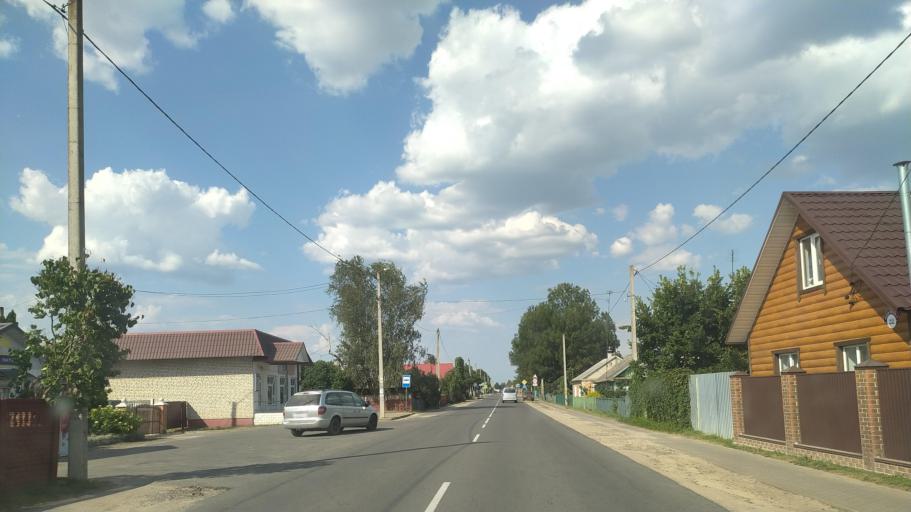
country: BY
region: Brest
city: Drahichyn
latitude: 52.1917
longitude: 25.1470
